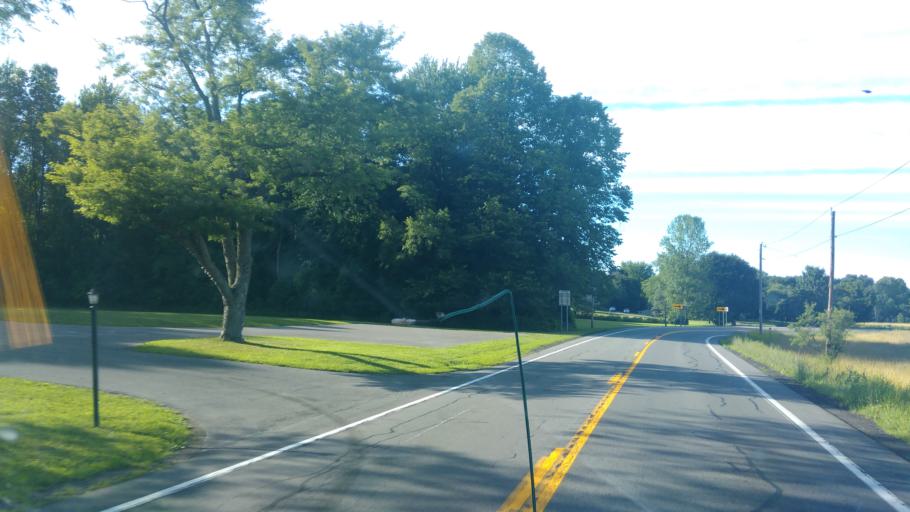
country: US
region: New York
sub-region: Wayne County
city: Lyons
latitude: 43.0802
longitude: -76.9902
